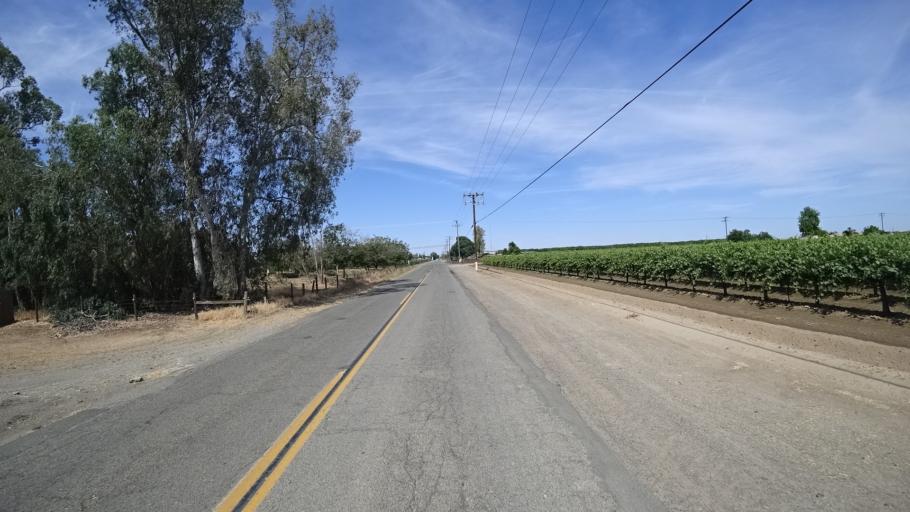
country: US
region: California
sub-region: Kings County
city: Hanford
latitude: 36.3571
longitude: -119.6086
